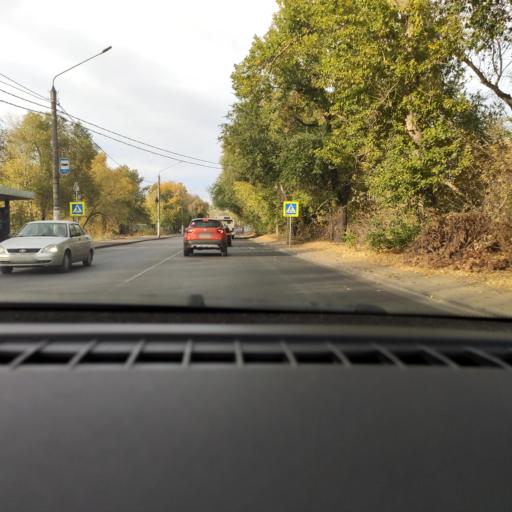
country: RU
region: Voronezj
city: Voronezh
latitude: 51.7295
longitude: 39.2599
